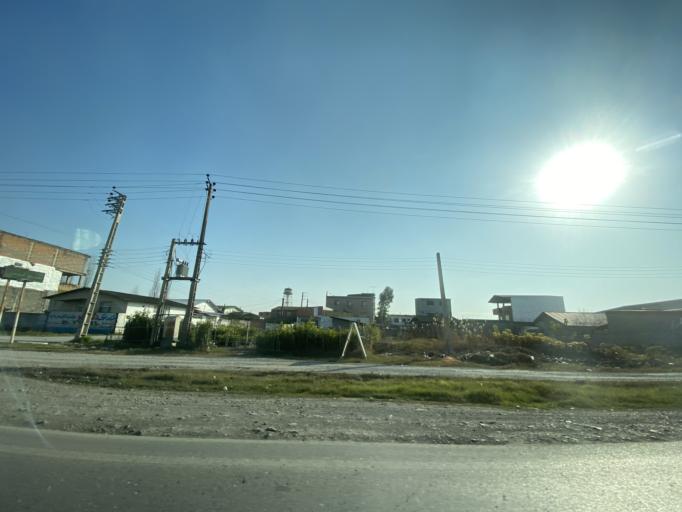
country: IR
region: Mazandaran
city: Babol
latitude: 36.5262
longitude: 52.6185
